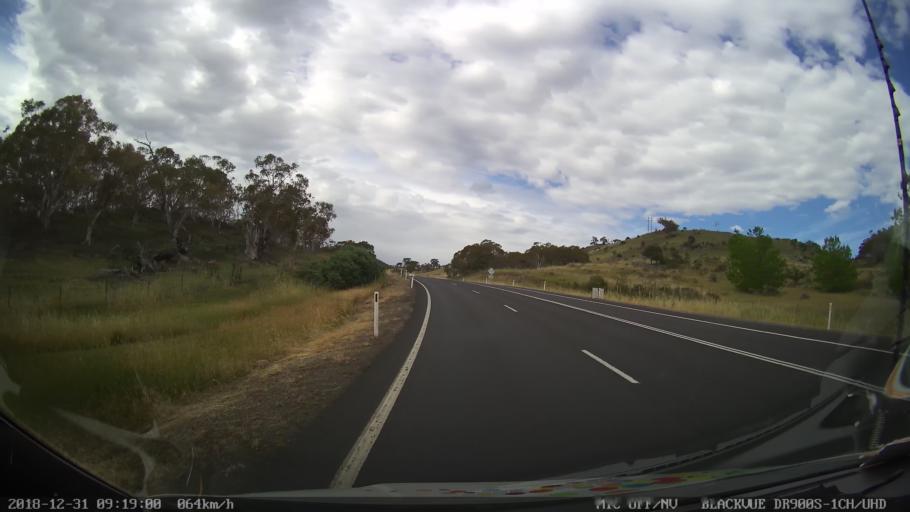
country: AU
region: New South Wales
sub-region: Snowy River
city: Jindabyne
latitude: -36.4118
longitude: 148.5885
